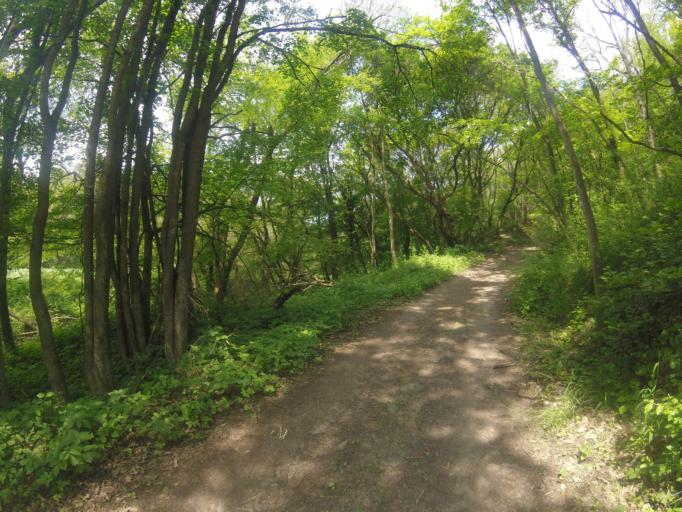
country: HU
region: Pest
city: Szob
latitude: 47.8220
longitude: 18.9146
